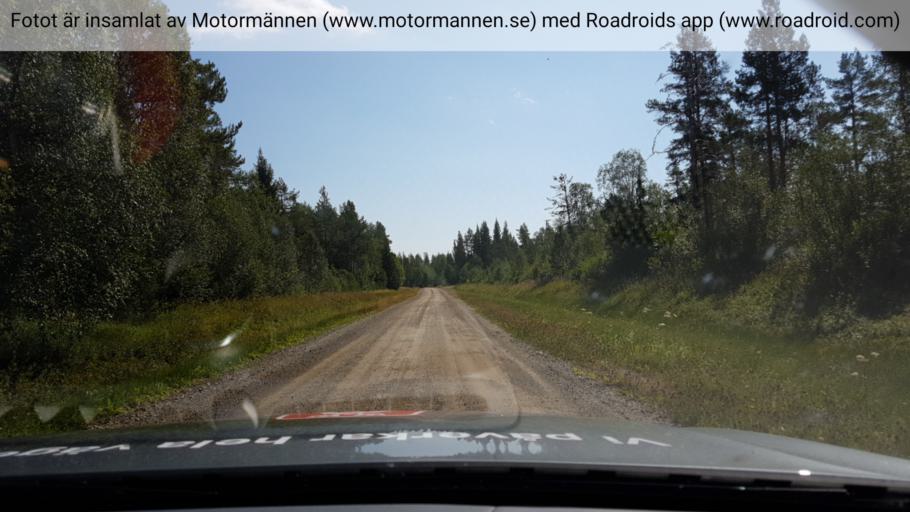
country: SE
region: Jaemtland
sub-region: Stroemsunds Kommun
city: Stroemsund
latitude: 63.3169
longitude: 15.4854
